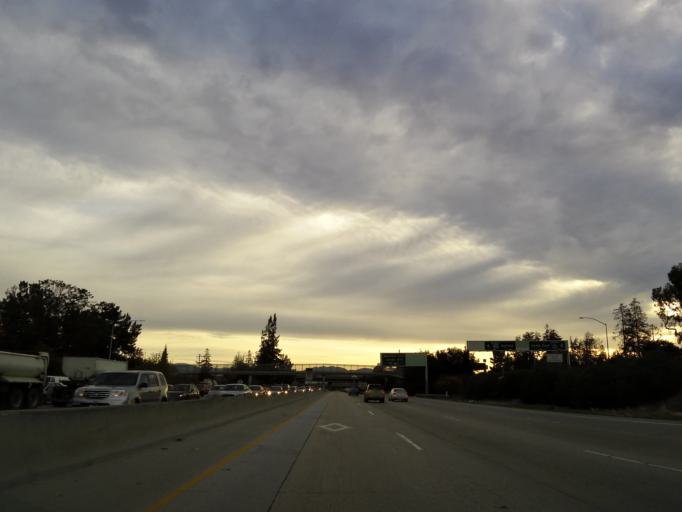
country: US
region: California
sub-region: Santa Clara County
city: Burbank
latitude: 37.3169
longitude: -121.9455
